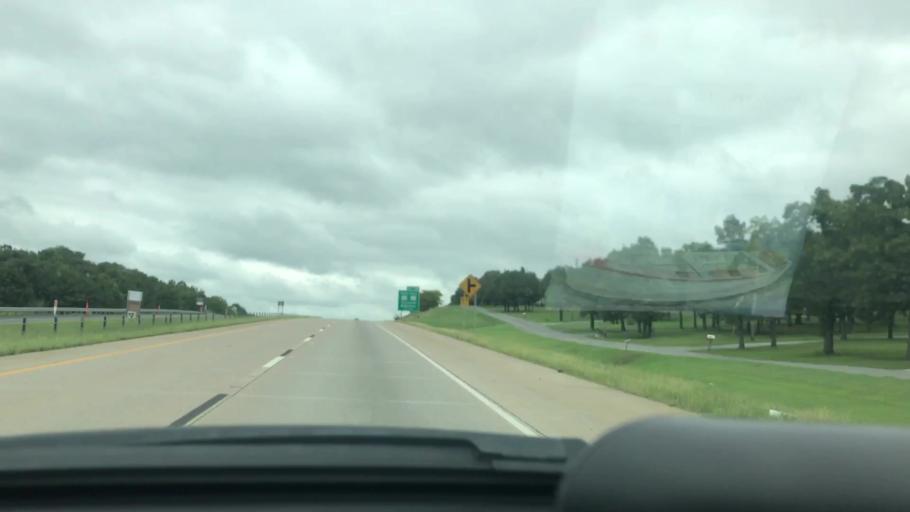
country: US
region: Oklahoma
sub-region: Pittsburg County
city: Krebs
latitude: 34.9865
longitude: -95.7221
